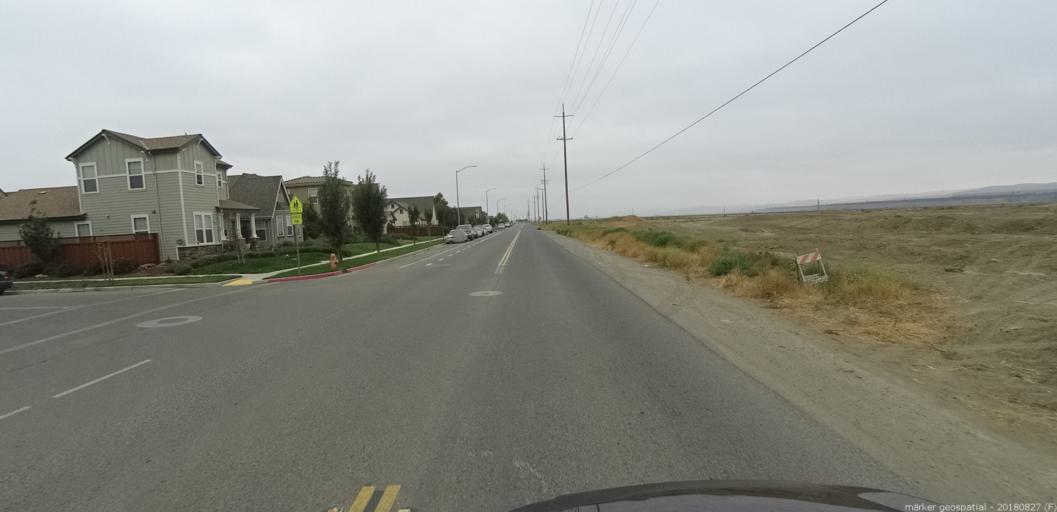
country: US
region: California
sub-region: Monterey County
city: King City
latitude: 36.2213
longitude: -121.1333
